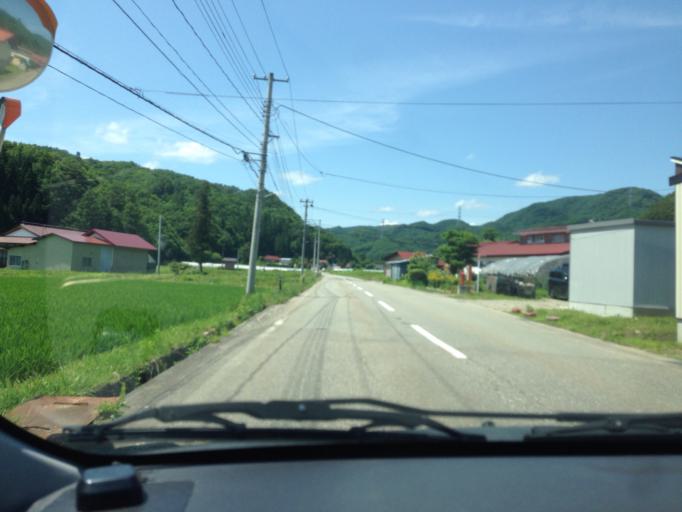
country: JP
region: Tochigi
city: Kuroiso
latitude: 37.2092
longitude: 139.7581
